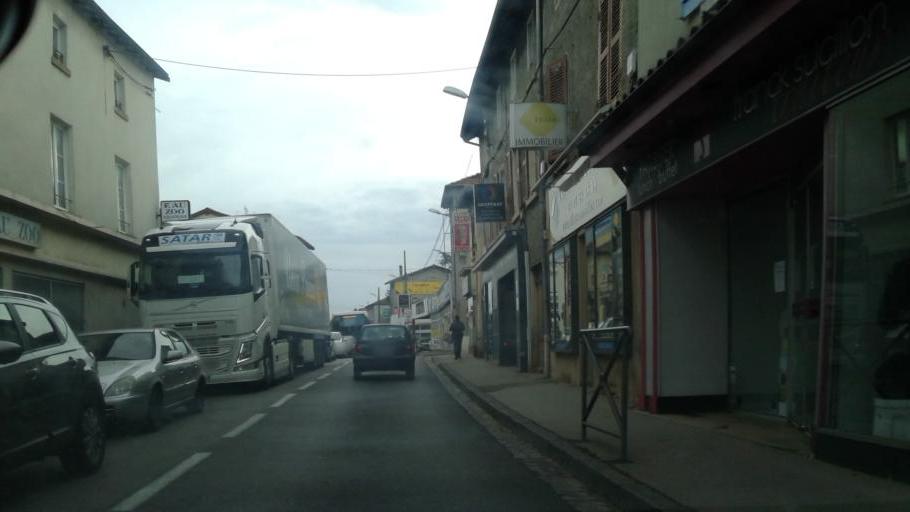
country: FR
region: Rhone-Alpes
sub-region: Departement du Rhone
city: Rillieux-la-Pape
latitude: 45.8209
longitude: 4.8977
